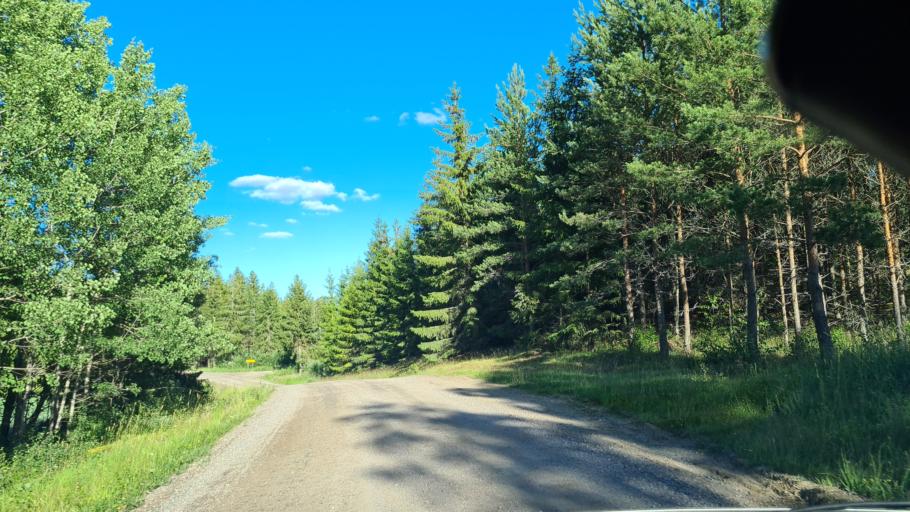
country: SE
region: Soedermanland
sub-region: Nykopings Kommun
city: Nykoping
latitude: 58.9201
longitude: 17.0361
